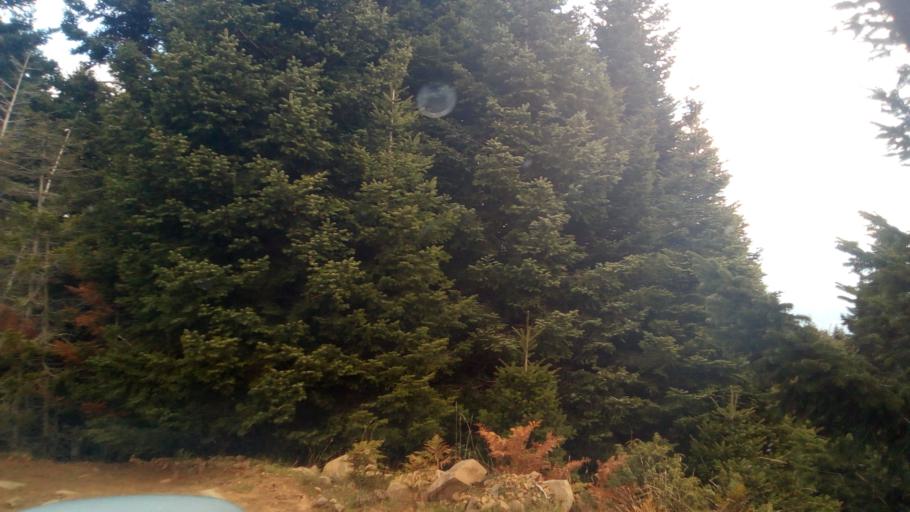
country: GR
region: Central Greece
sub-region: Nomos Fokidos
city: Lidoriki
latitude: 38.6100
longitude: 21.9693
